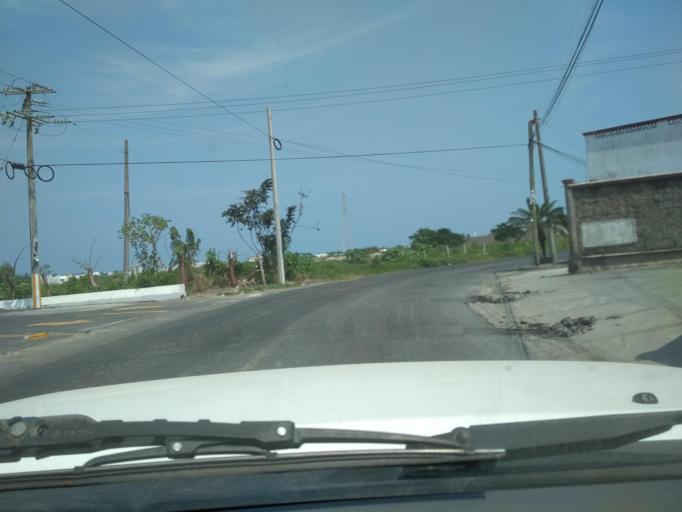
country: MX
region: Veracruz
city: Boca del Rio
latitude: 19.0961
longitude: -96.1231
